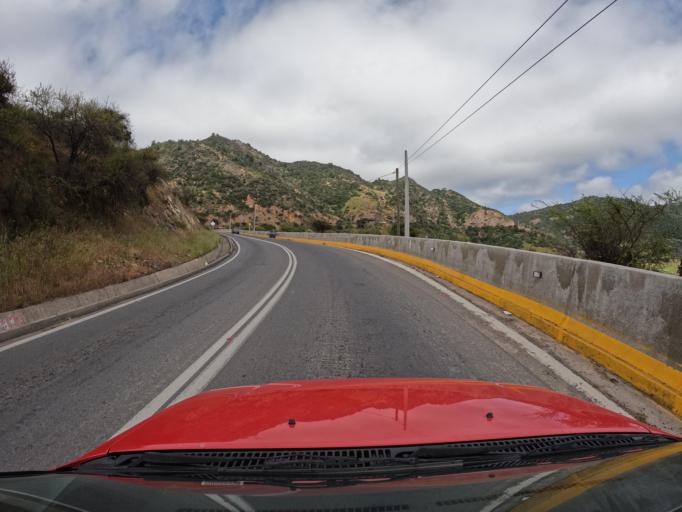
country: CL
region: O'Higgins
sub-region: Provincia de Colchagua
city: Santa Cruz
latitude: -34.6614
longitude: -71.4152
